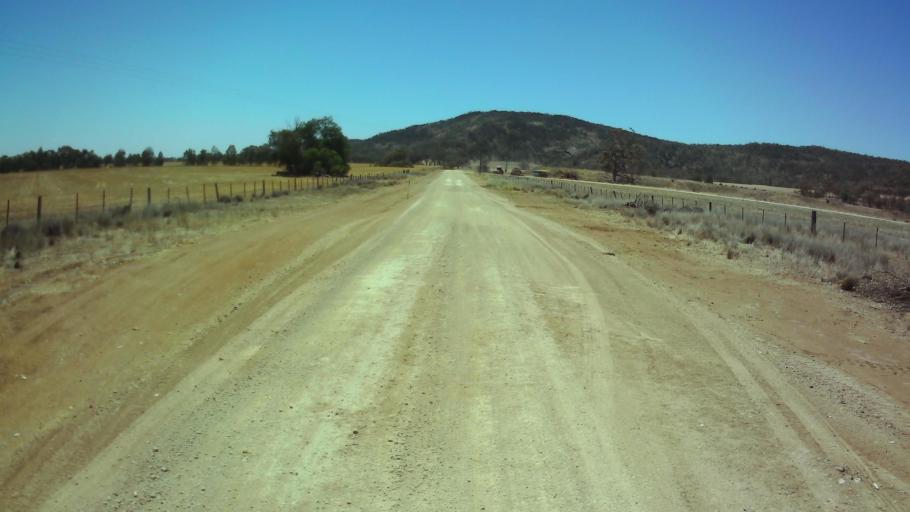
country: AU
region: New South Wales
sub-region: Weddin
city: Grenfell
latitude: -33.8588
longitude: 148.1072
